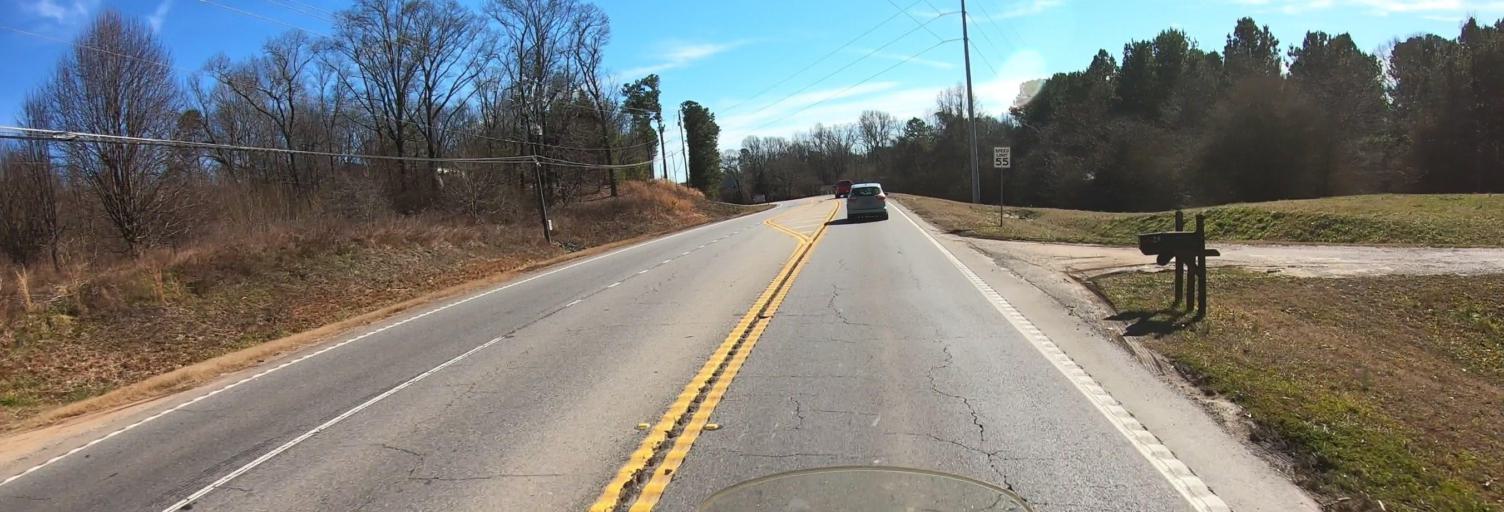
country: US
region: Georgia
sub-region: Forsyth County
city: Cumming
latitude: 34.2831
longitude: -84.1302
